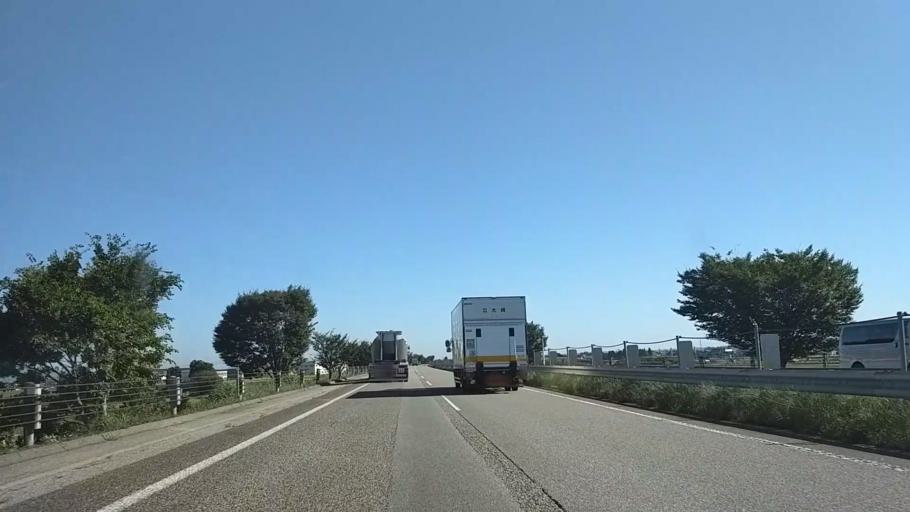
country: JP
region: Toyama
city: Nanto-shi
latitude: 36.6408
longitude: 136.9742
